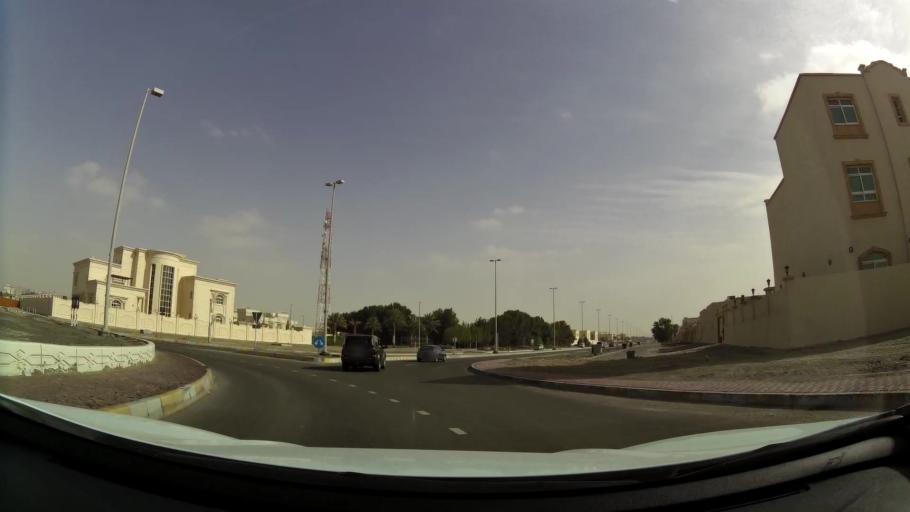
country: AE
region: Abu Dhabi
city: Abu Dhabi
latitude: 24.4152
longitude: 54.6020
